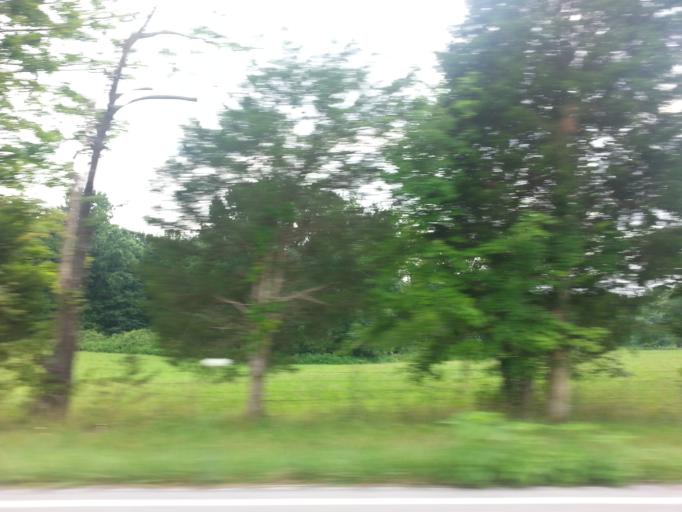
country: US
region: Kentucky
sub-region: Robertson County
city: Mount Olivet
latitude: 38.4974
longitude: -84.1331
